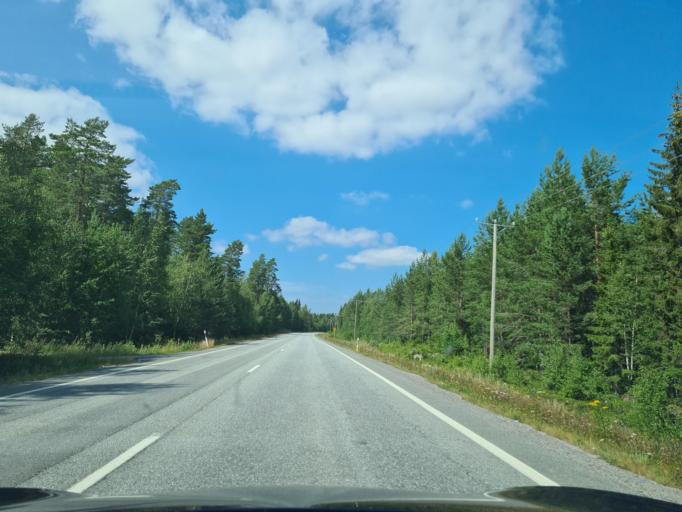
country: FI
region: Ostrobothnia
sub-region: Vaasa
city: Vaasa
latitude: 63.1699
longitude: 21.5846
